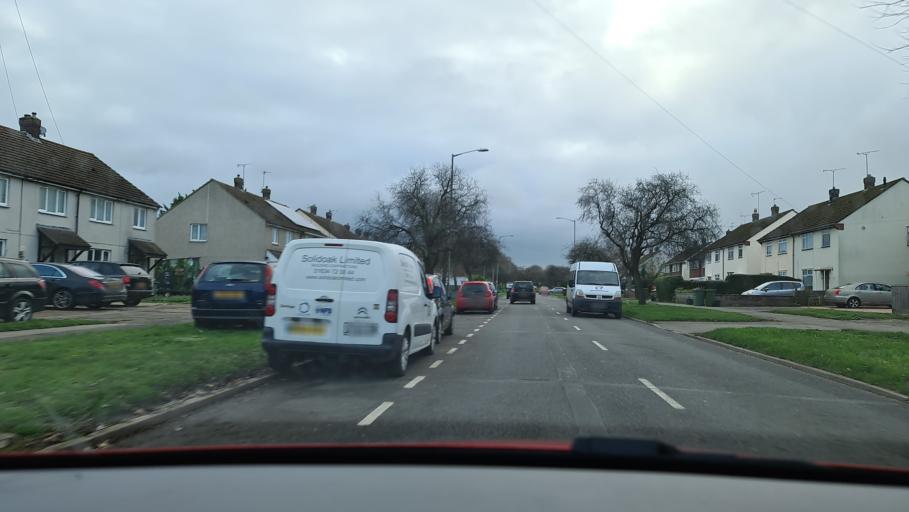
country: GB
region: England
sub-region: Buckinghamshire
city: Aylesbury
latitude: 51.8028
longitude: -0.8161
